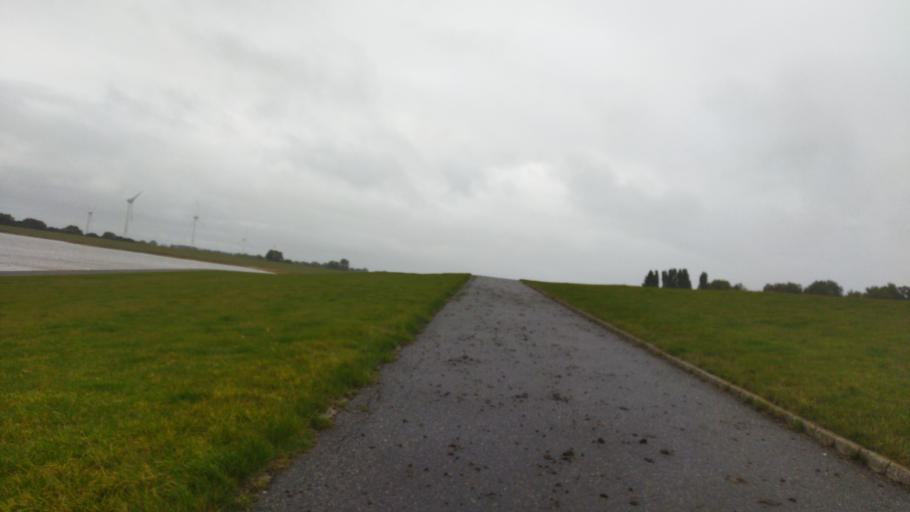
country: NL
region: Groningen
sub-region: Gemeente Delfzijl
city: Delfzijl
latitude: 53.3365
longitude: 7.0560
